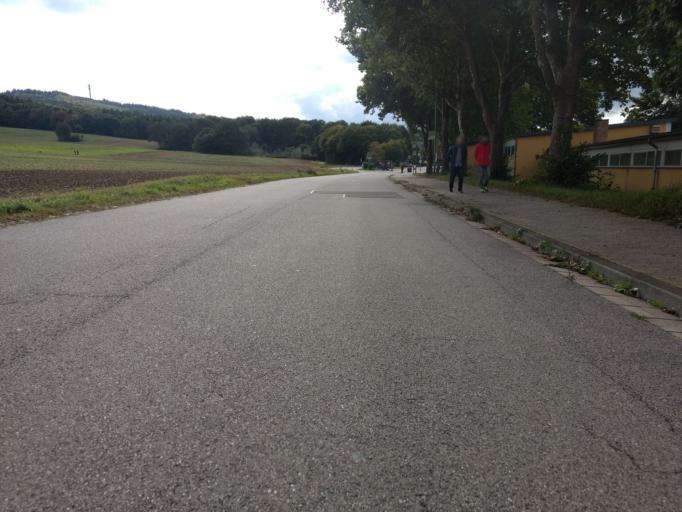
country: DE
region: Saarland
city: Lebach
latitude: 49.4028
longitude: 6.8975
